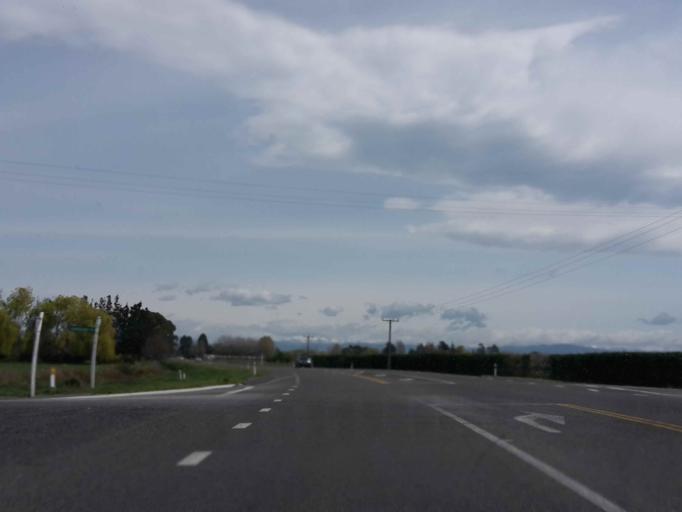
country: NZ
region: Canterbury
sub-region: Waimakariri District
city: Kaiapoi
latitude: -43.3976
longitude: 172.6057
